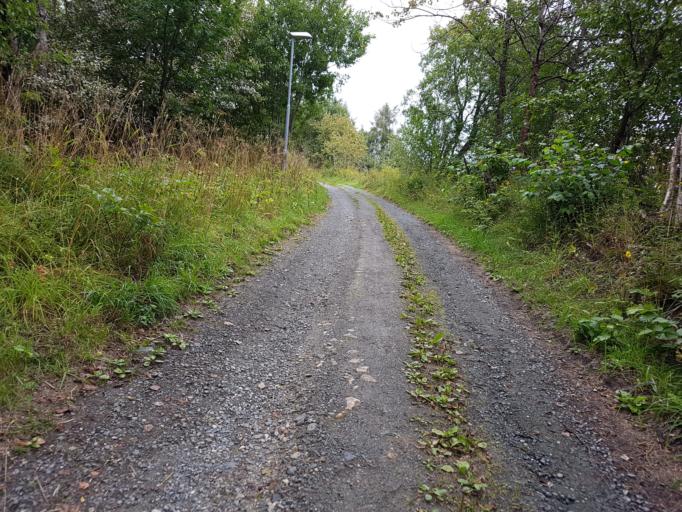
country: NO
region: Sor-Trondelag
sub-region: Trondheim
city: Trondheim
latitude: 63.3852
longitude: 10.3580
